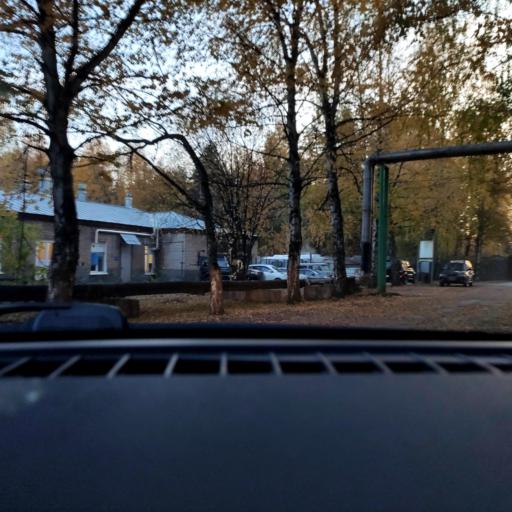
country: RU
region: Perm
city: Kondratovo
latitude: 57.9761
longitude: 56.1479
